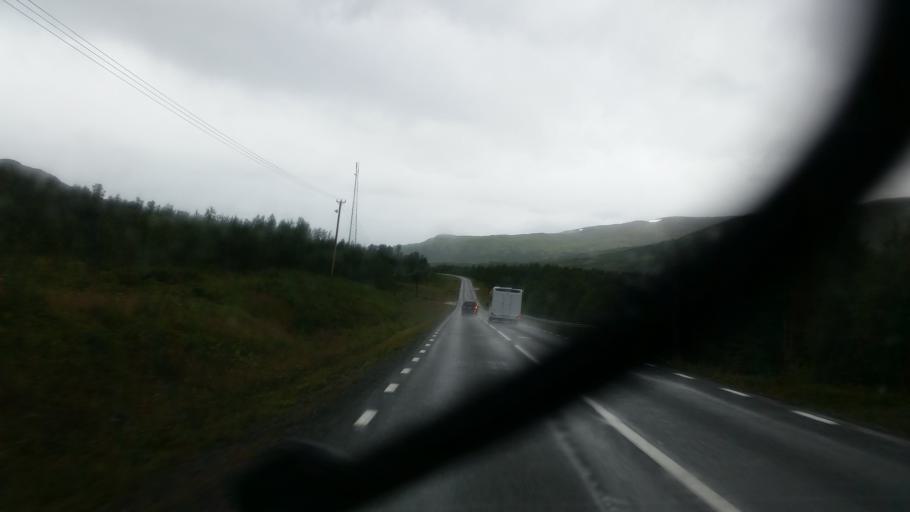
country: NO
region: Nordland
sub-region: Rana
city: Mo i Rana
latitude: 65.9155
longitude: 14.9947
